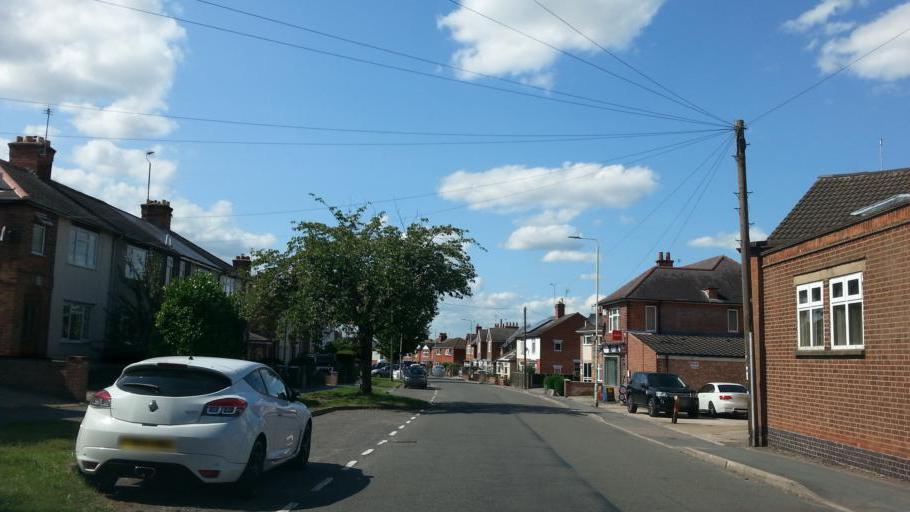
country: GB
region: England
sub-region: Leicestershire
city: Sileby
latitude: 52.7314
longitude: -1.0996
